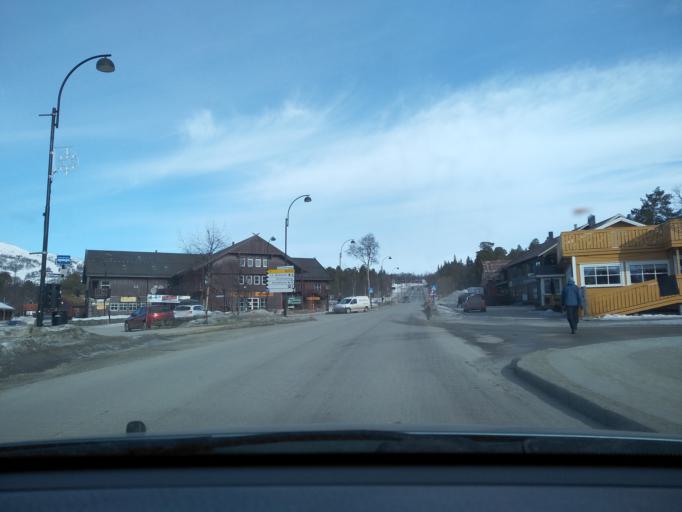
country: NO
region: Aust-Agder
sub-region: Bykle
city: Hovden
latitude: 59.5599
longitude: 7.3567
